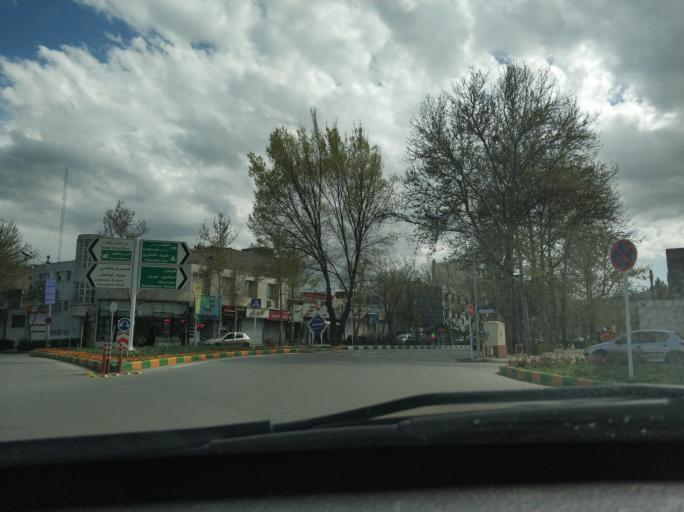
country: IR
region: Razavi Khorasan
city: Mashhad
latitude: 36.2747
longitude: 59.5915
